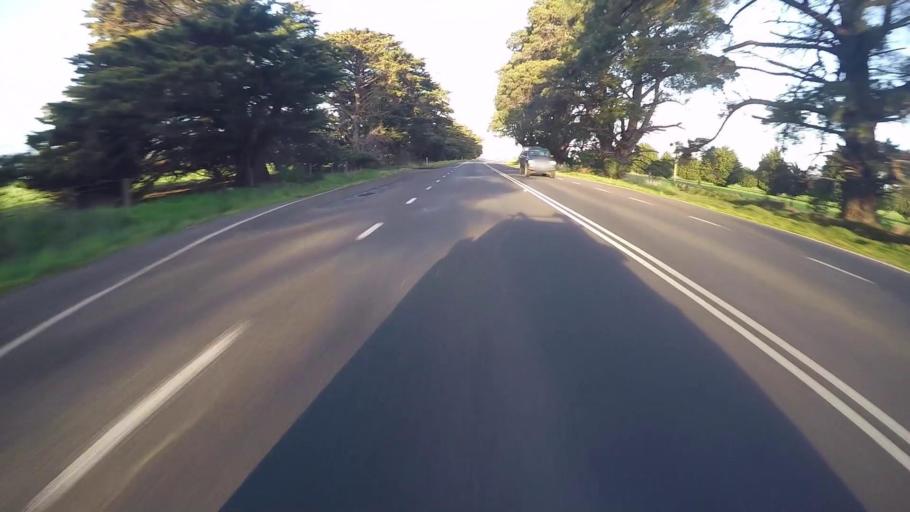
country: AU
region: Victoria
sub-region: Greater Geelong
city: Wandana Heights
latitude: -38.1240
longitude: 144.2331
